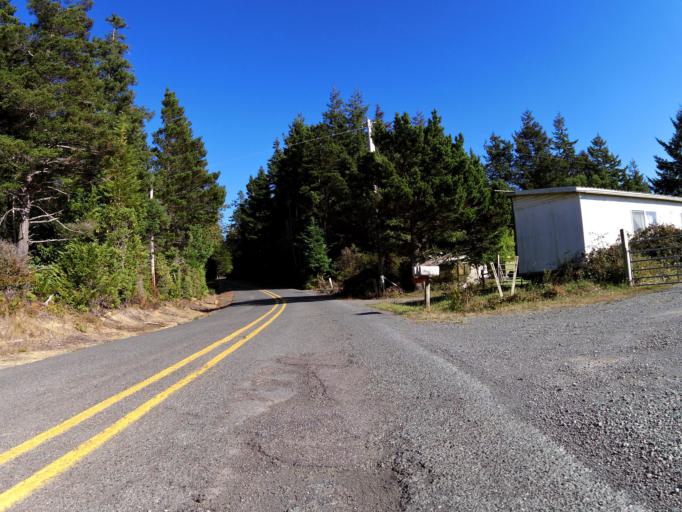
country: US
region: Oregon
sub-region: Coos County
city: Bandon
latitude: 43.0394
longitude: -124.4016
